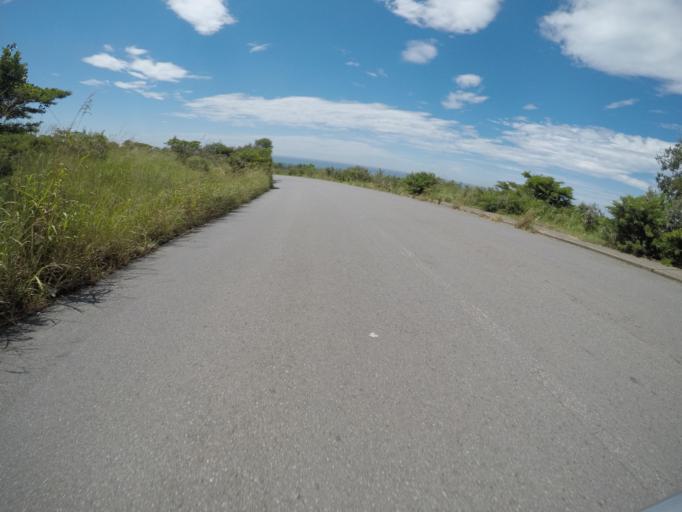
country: ZA
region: Eastern Cape
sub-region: Buffalo City Metropolitan Municipality
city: East London
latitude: -33.0416
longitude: 27.8701
